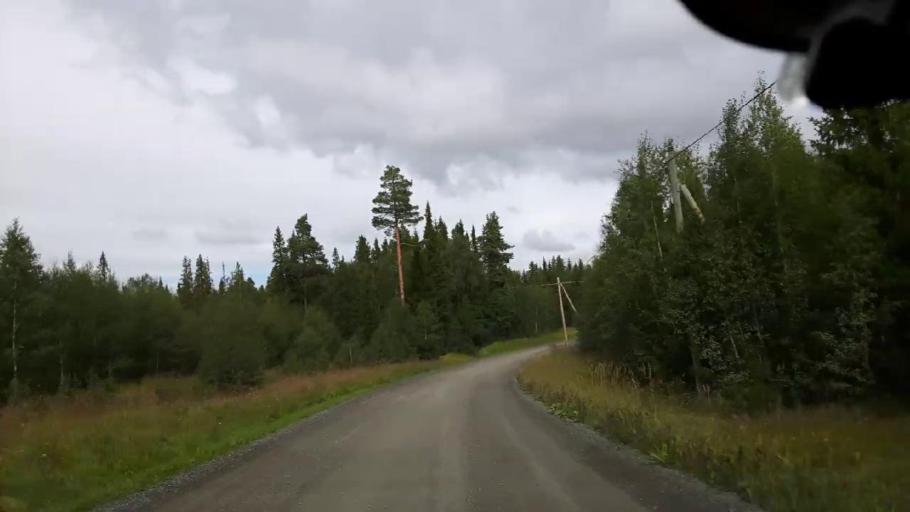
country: SE
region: Jaemtland
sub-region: Krokoms Kommun
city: Valla
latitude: 63.4019
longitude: 14.0944
